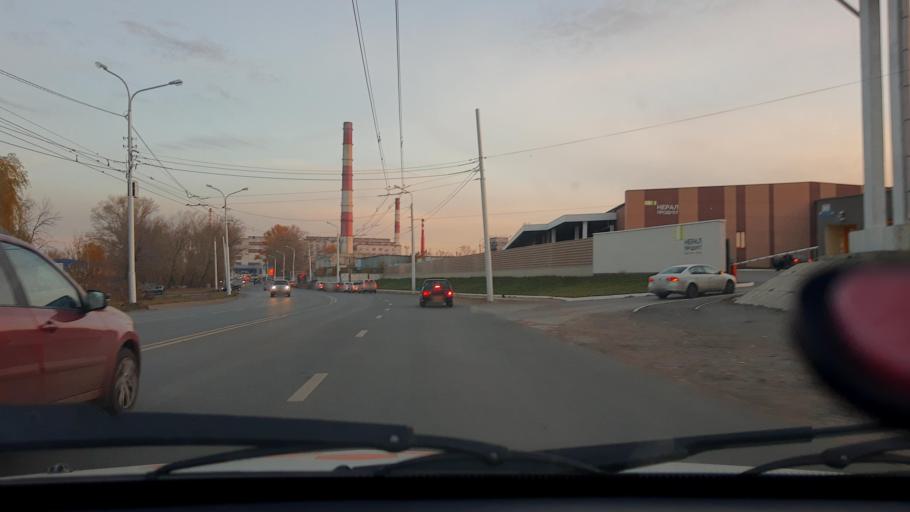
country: RU
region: Bashkortostan
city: Ufa
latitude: 54.8333
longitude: 56.0895
